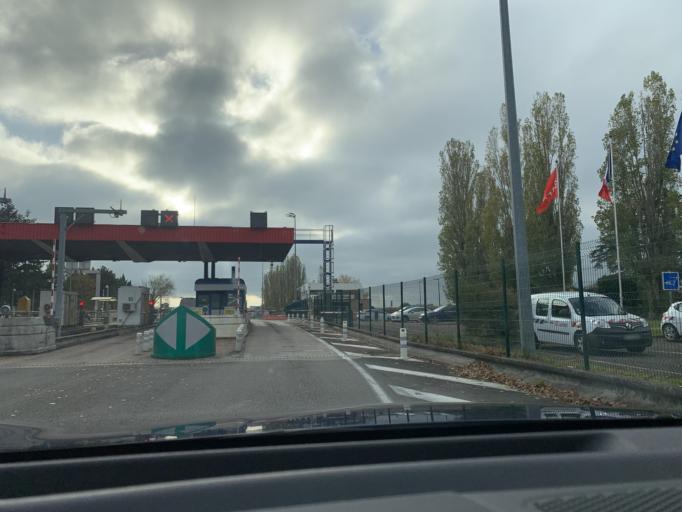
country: FR
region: Bourgogne
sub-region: Departement de Saone-et-Loire
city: Saint-Martin-Belle-Roche
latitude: 46.3663
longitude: 4.8387
